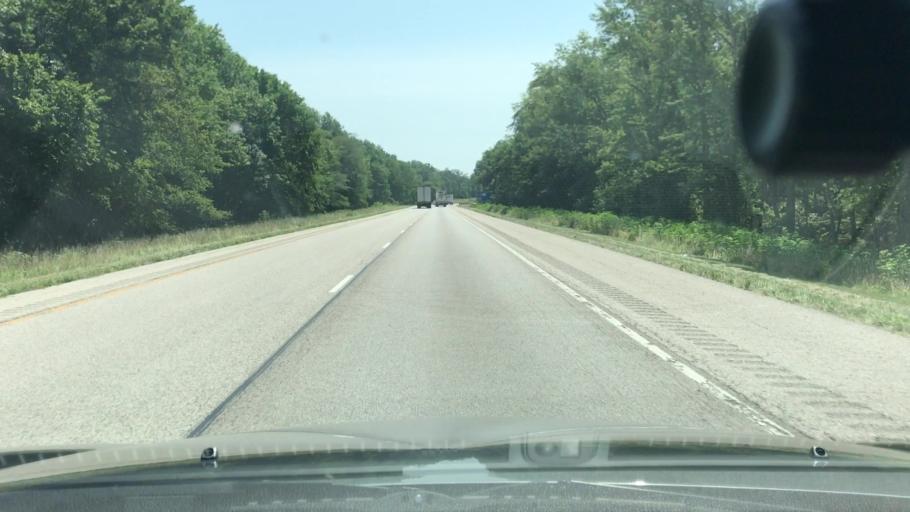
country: US
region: Illinois
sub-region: Washington County
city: Nashville
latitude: 38.4003
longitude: -89.3987
